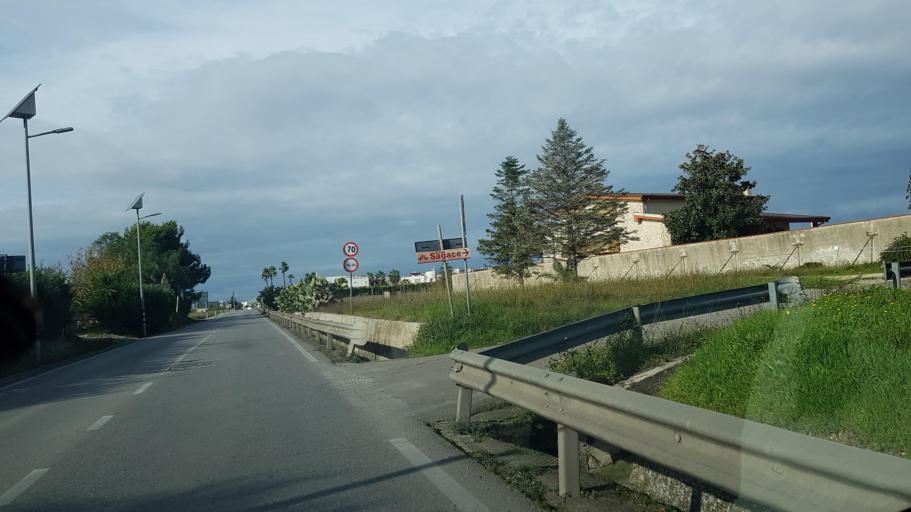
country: IT
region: Apulia
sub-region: Provincia di Brindisi
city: Oria
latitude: 40.4904
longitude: 17.6420
